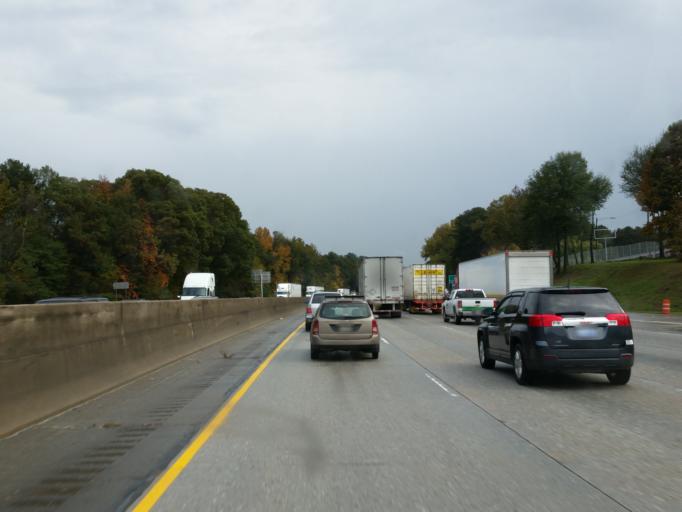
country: US
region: Georgia
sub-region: Fulton County
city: College Park
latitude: 33.6340
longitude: -84.4907
